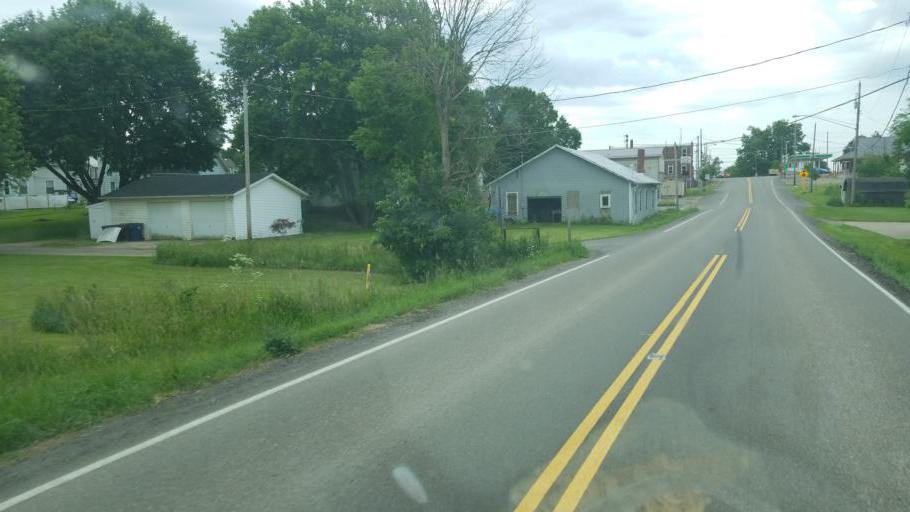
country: US
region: Ohio
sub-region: Knox County
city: Danville
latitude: 40.4528
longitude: -82.2600
